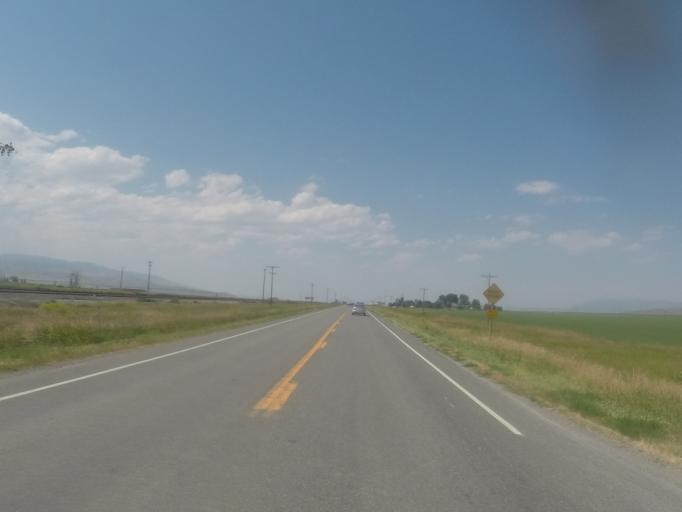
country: US
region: Montana
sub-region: Broadwater County
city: Townsend
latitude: 46.1818
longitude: -111.4450
